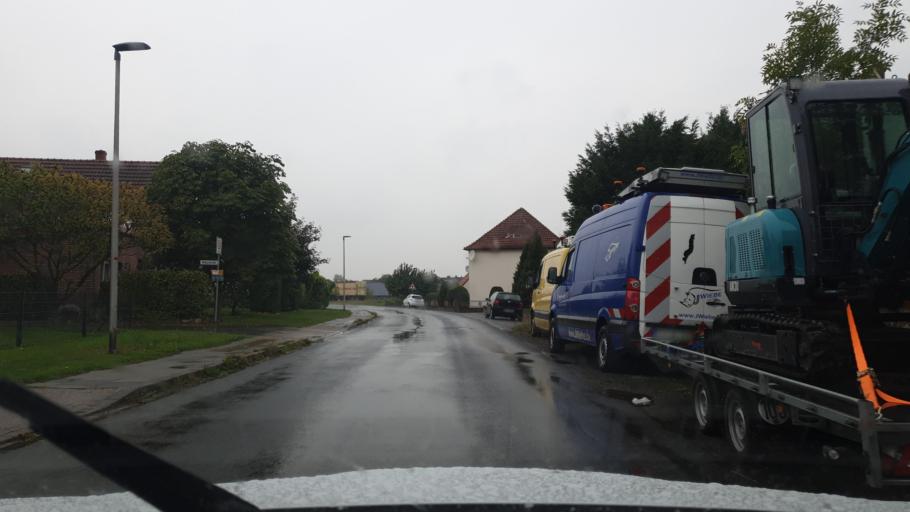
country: DE
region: North Rhine-Westphalia
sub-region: Regierungsbezirk Detmold
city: Vlotho
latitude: 52.2162
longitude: 8.8704
